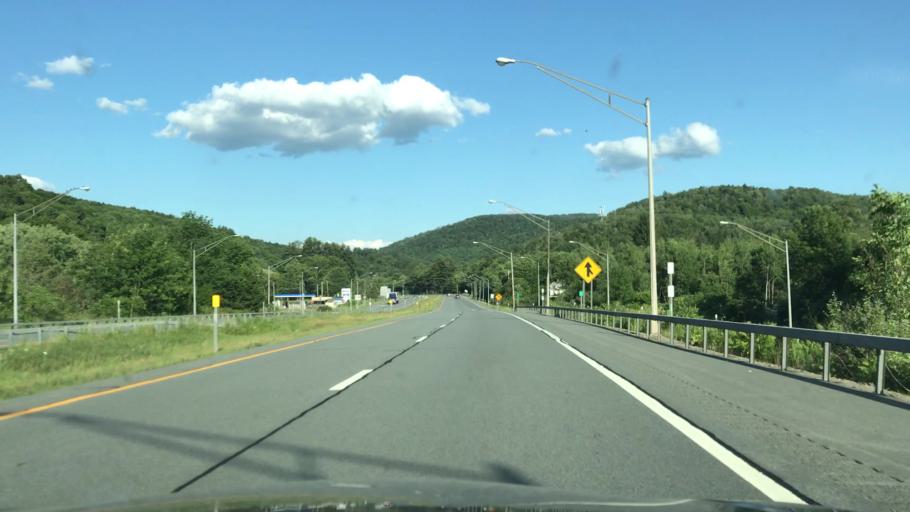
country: US
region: New York
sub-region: Sullivan County
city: Livingston Manor
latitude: 41.9309
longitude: -74.9131
